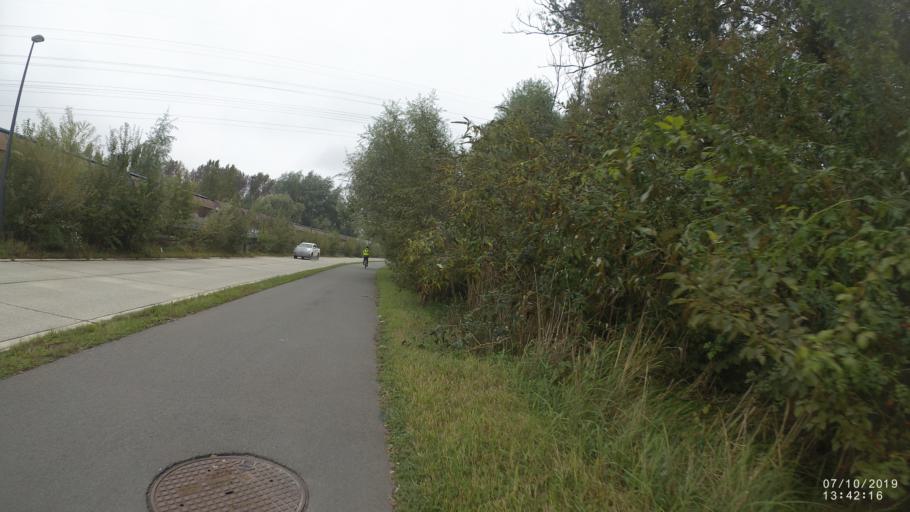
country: BE
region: Flanders
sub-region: Provincie Oost-Vlaanderen
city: Gent
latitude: 51.0737
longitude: 3.7199
